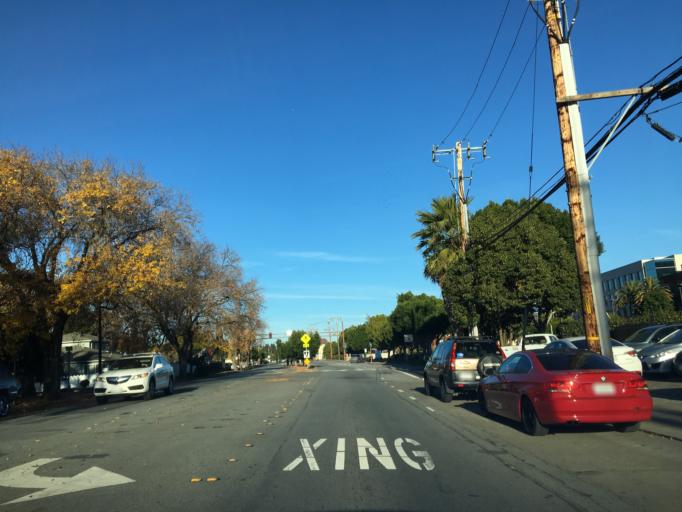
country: US
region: California
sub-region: San Mateo County
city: Redwood City
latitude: 37.4972
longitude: -122.2397
